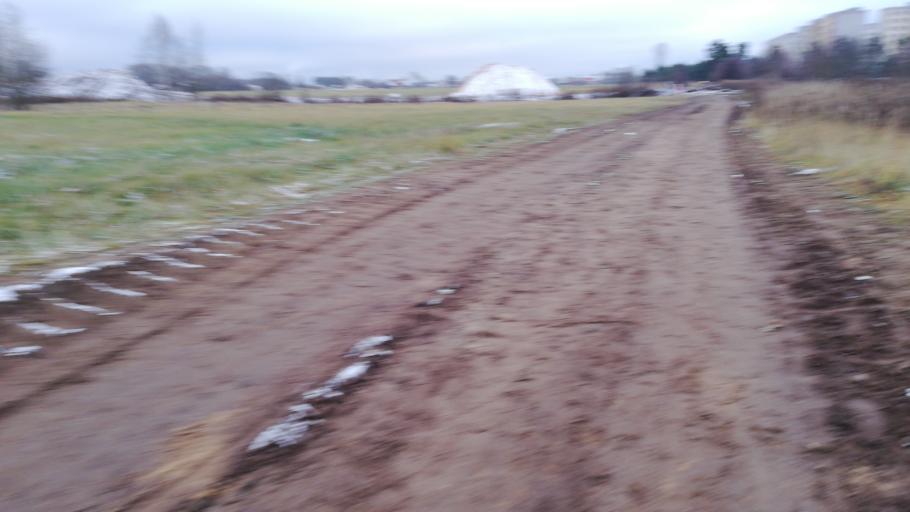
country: LV
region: Stopini
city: Ulbroka
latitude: 56.9501
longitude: 24.2376
